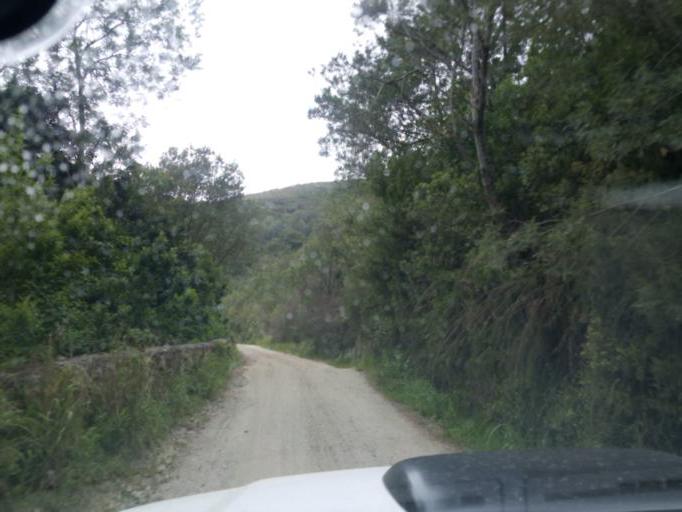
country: ZA
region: Western Cape
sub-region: Eden District Municipality
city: George
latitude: -33.8885
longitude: 22.4300
